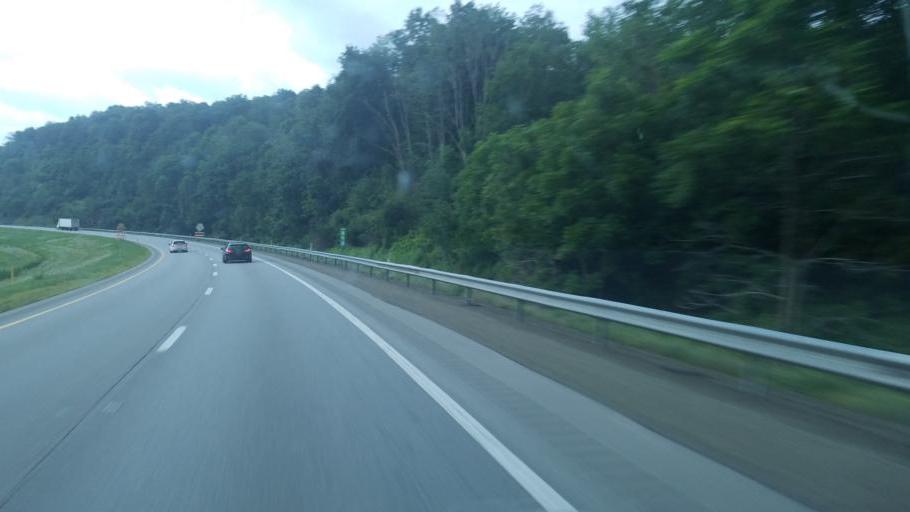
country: US
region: Pennsylvania
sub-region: Butler County
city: Zelienople
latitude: 40.8371
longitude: -80.1051
